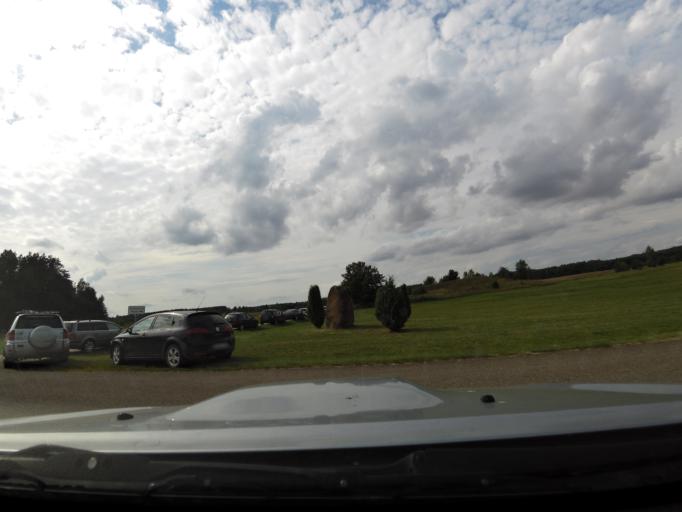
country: LT
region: Vilnius County
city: Elektrenai
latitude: 54.8379
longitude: 24.5656
